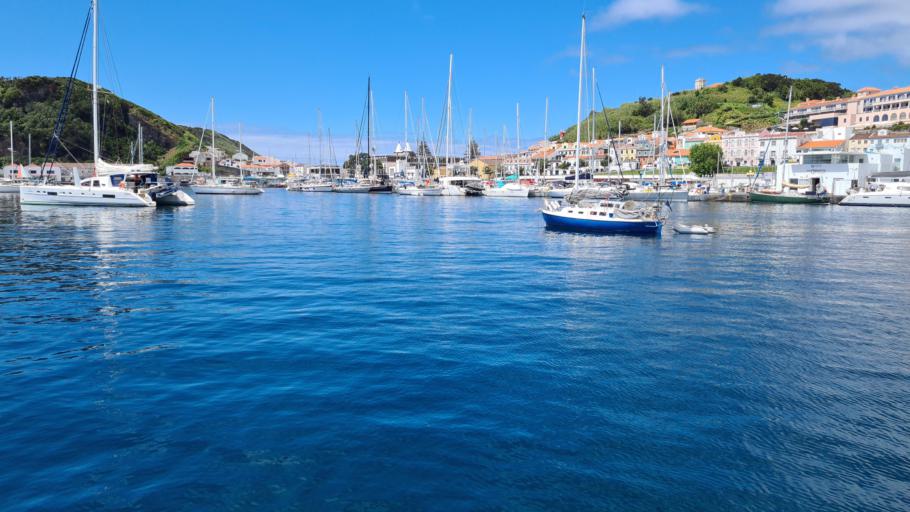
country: PT
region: Azores
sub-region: Horta
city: Horta
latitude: 38.5315
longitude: -28.6242
